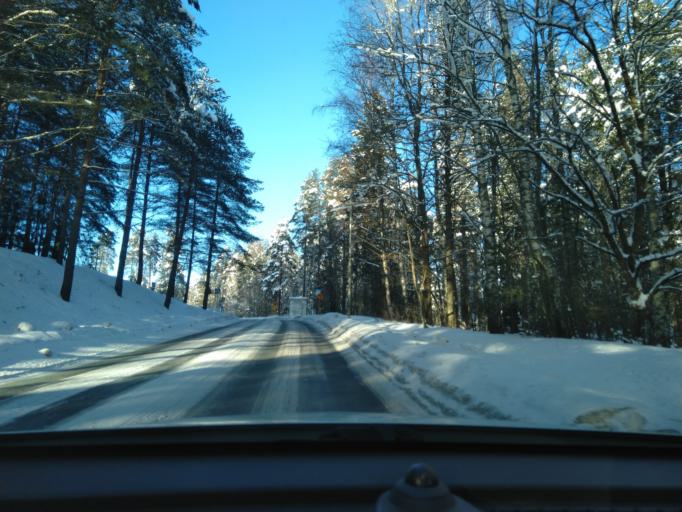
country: FI
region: Haeme
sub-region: Haemeenlinna
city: Haemeenlinna
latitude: 60.9880
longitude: 24.4175
